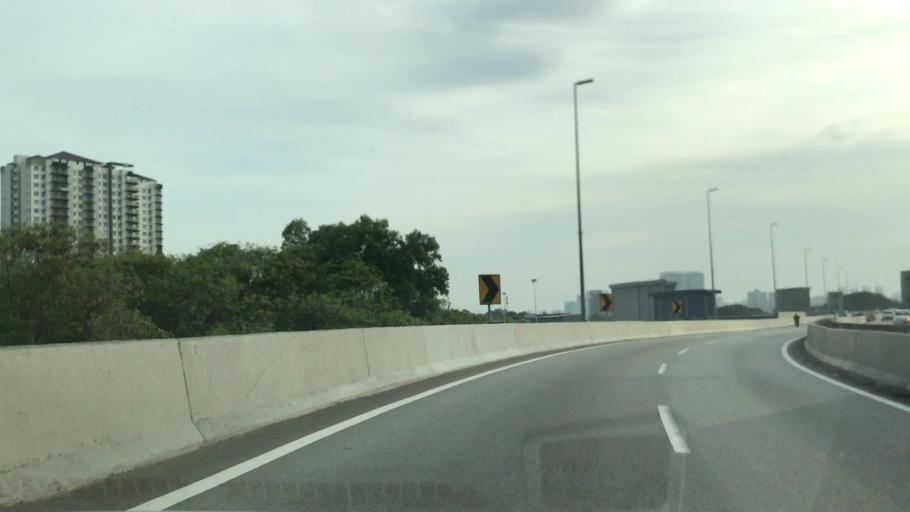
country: MY
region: Kuala Lumpur
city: Kuala Lumpur
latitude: 3.1145
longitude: 101.7166
